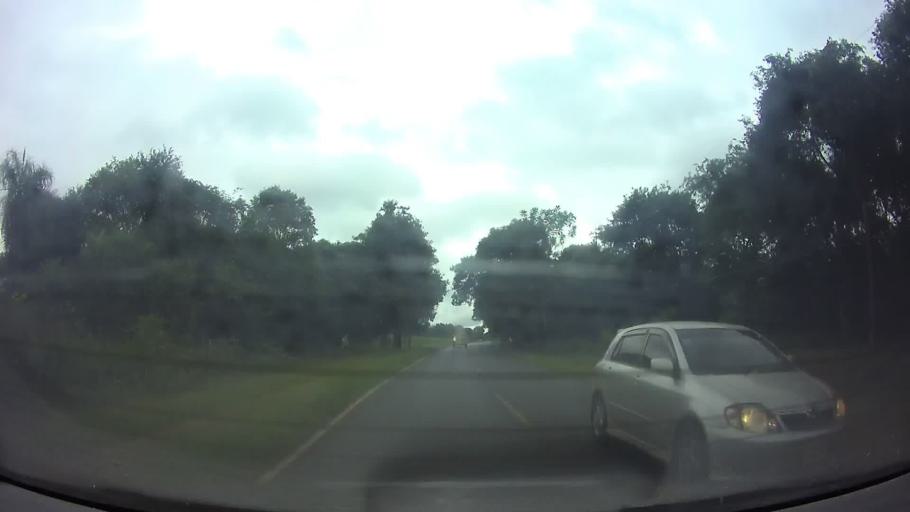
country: PY
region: Central
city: Guarambare
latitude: -25.5401
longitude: -57.5004
